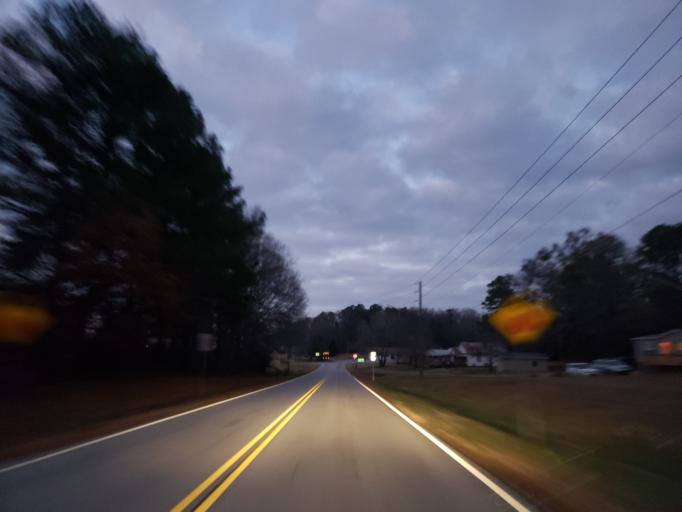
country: US
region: Georgia
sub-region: Carroll County
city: Temple
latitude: 33.8263
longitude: -85.0446
